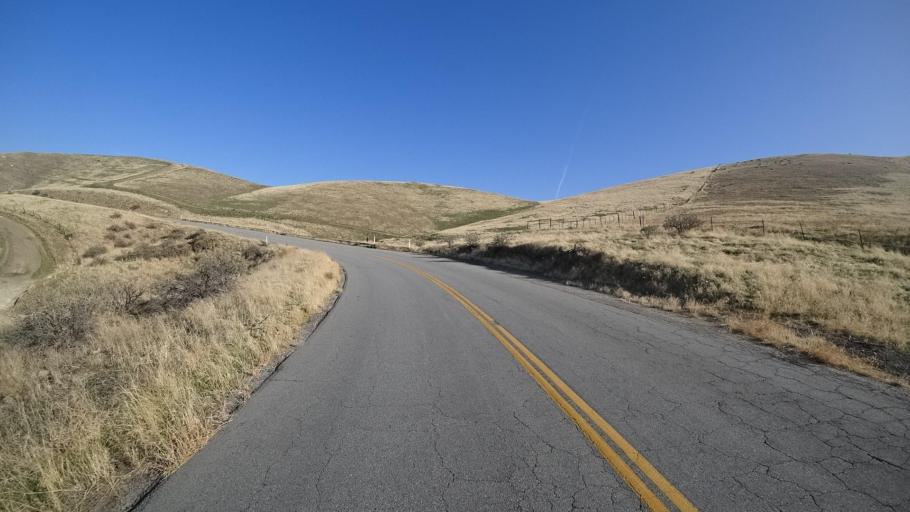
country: US
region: California
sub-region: Kern County
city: Bear Valley Springs
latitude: 35.2764
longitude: -118.6941
